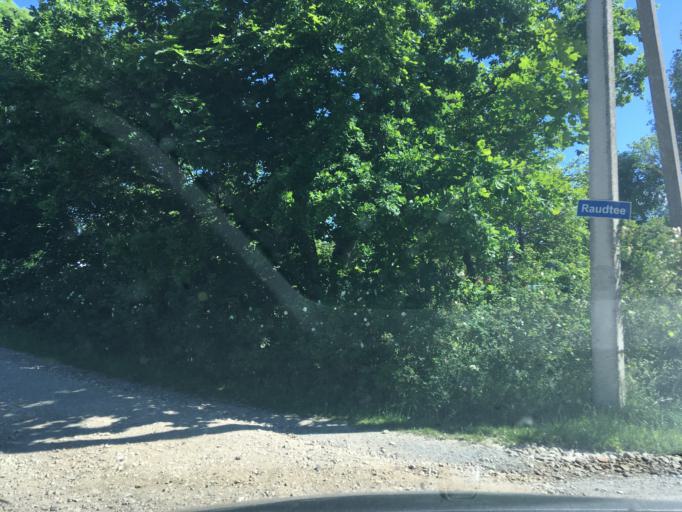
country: EE
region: Harju
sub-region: Raasiku vald
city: Raasiku
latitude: 59.3652
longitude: 25.1741
